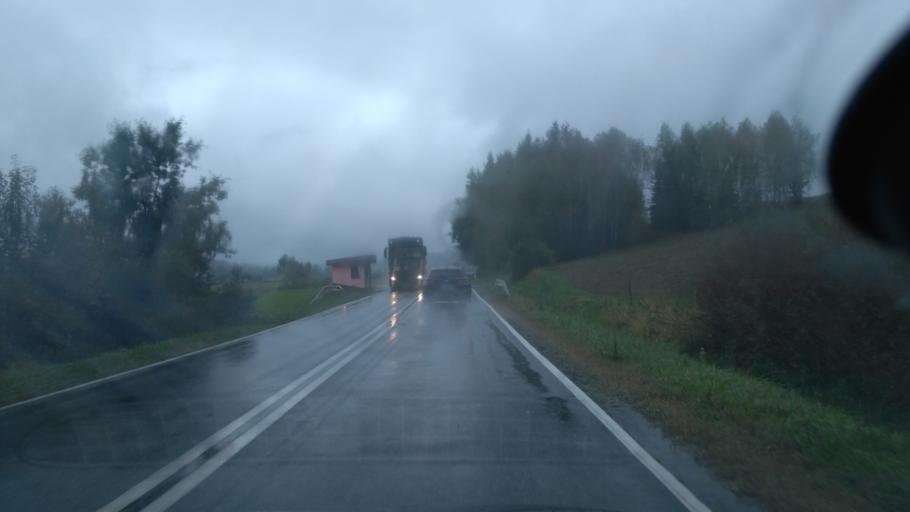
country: PL
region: Subcarpathian Voivodeship
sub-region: Powiat ropczycko-sedziszowski
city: Niedzwiada
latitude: 49.9800
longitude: 21.5595
